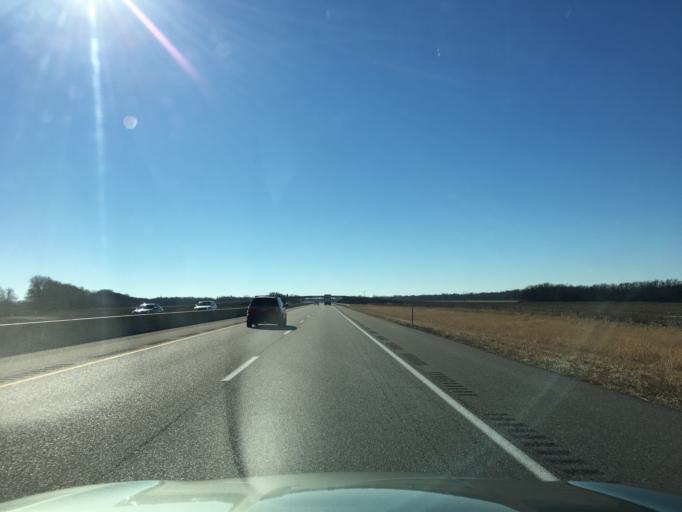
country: US
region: Kansas
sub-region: Sumner County
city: Belle Plaine
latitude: 37.4117
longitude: -97.3223
